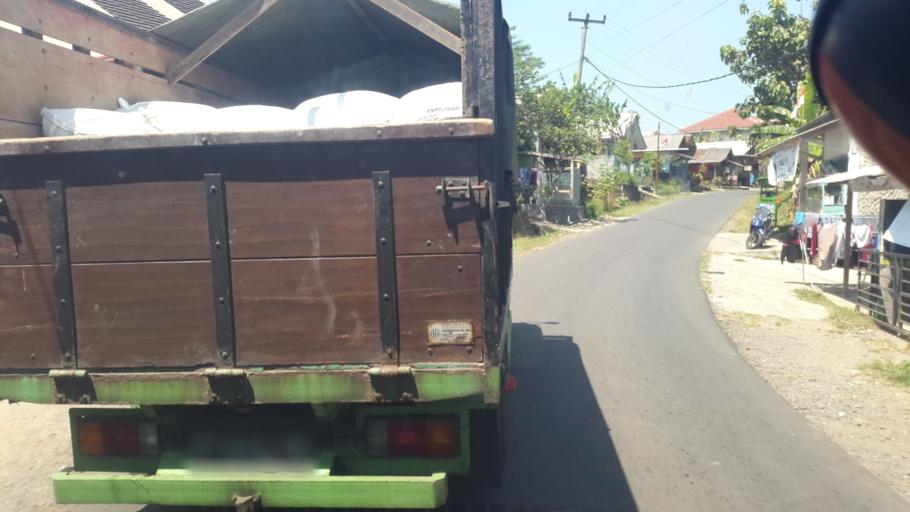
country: ID
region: Banten
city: Kubang
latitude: -6.7969
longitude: 106.6230
